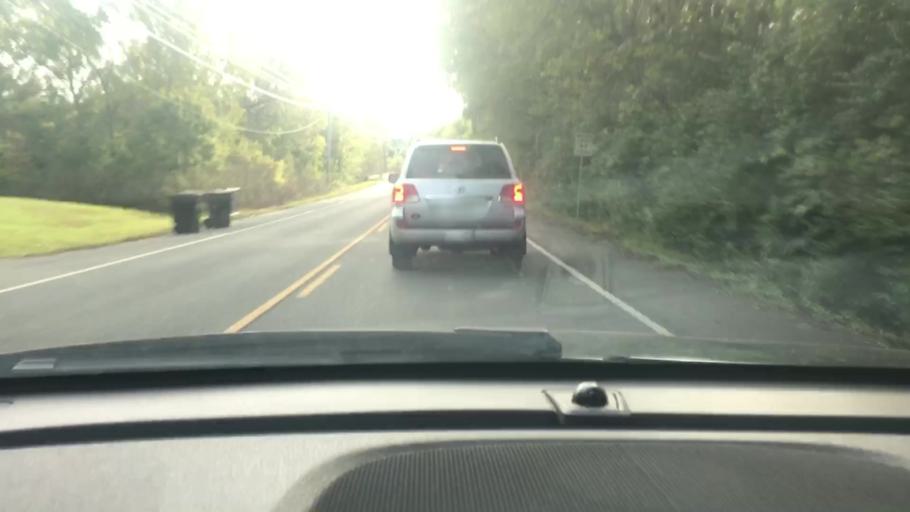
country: US
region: Tennessee
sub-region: Williamson County
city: Franklin
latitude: 35.9442
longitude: -86.8539
